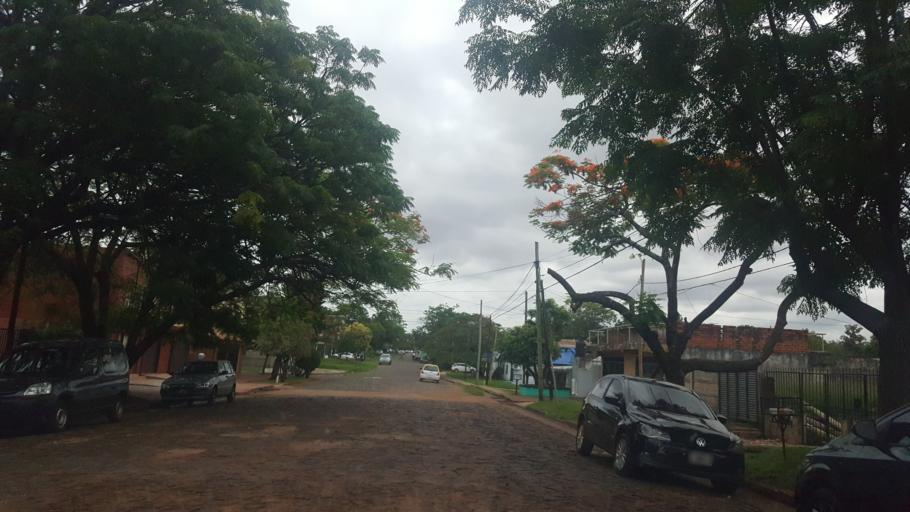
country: AR
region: Misiones
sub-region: Departamento de Capital
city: Posadas
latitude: -27.3680
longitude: -55.9096
